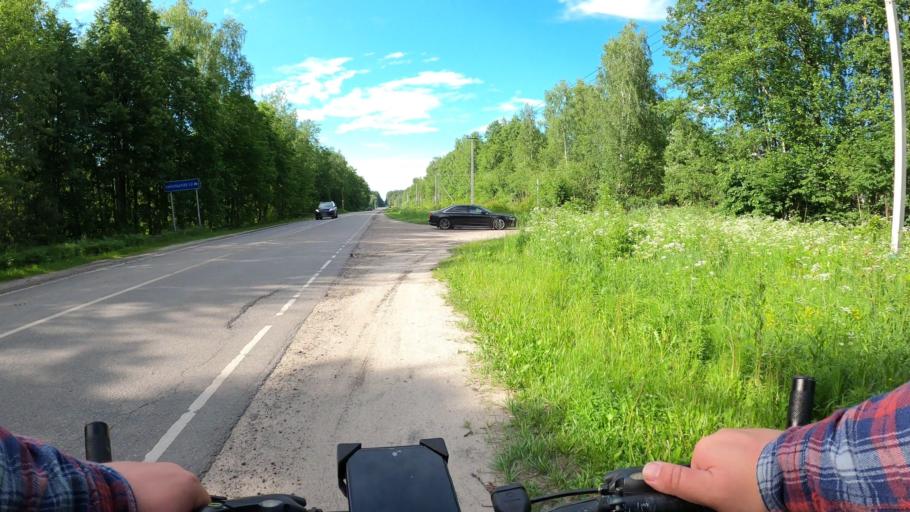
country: RU
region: Moskovskaya
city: Konobeyevo
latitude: 55.4301
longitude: 38.6621
